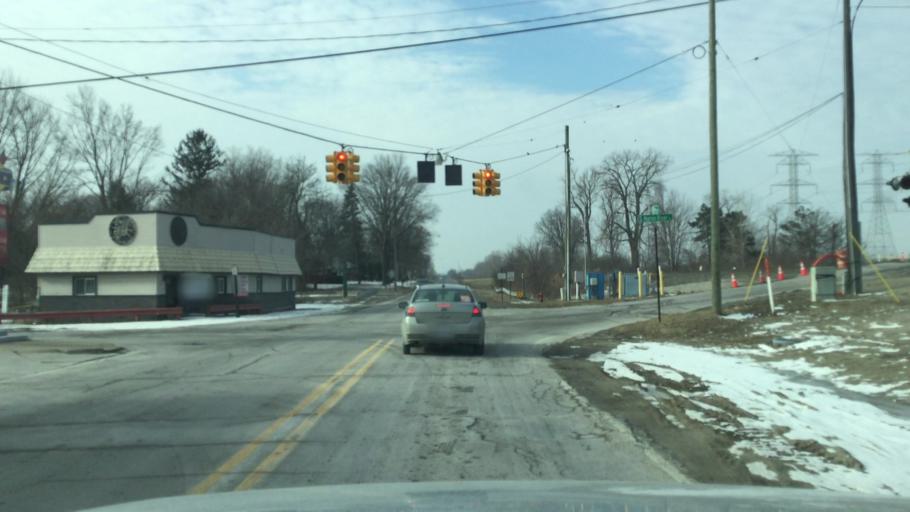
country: US
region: Michigan
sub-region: Monroe County
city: South Rockwood
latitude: 42.0624
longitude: -83.2555
